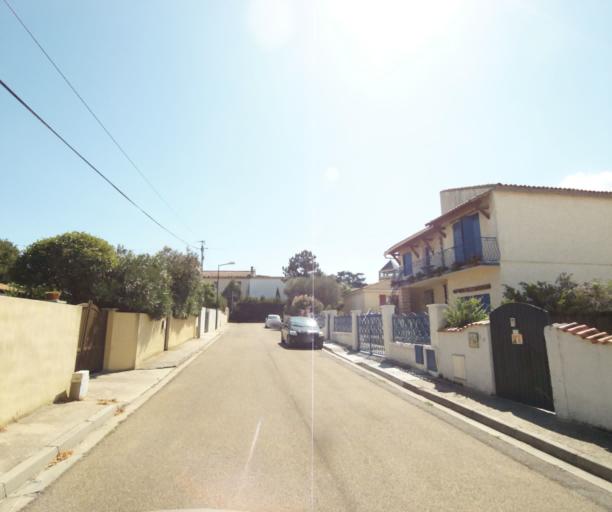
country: FR
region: Languedoc-Roussillon
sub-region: Departement du Gard
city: Bouillargues
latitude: 43.8025
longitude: 4.4236
